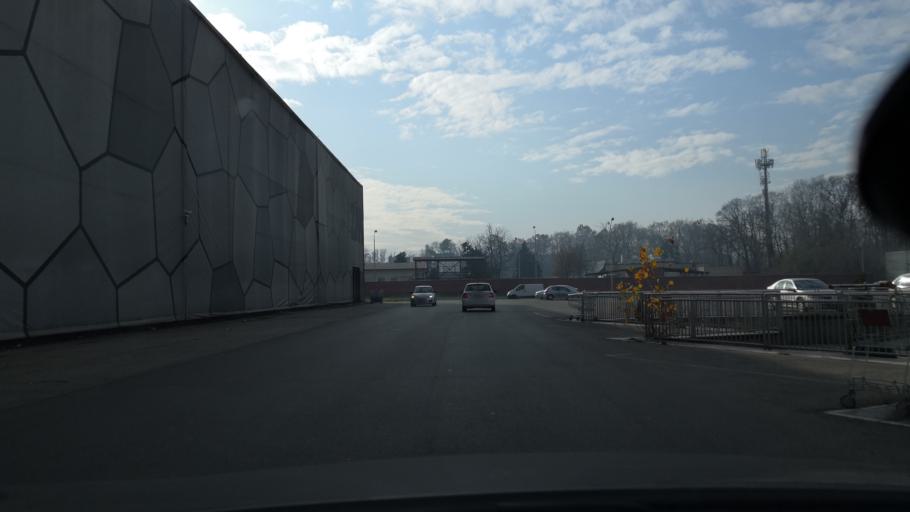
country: RS
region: Central Serbia
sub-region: Belgrade
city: Zemun
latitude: 44.8334
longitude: 20.3700
